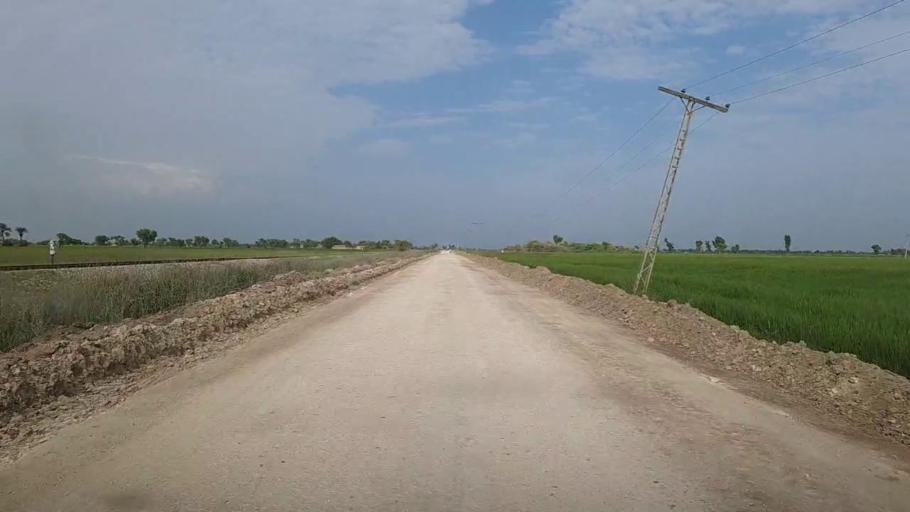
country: PK
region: Sindh
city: Thul
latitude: 28.2614
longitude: 68.8170
